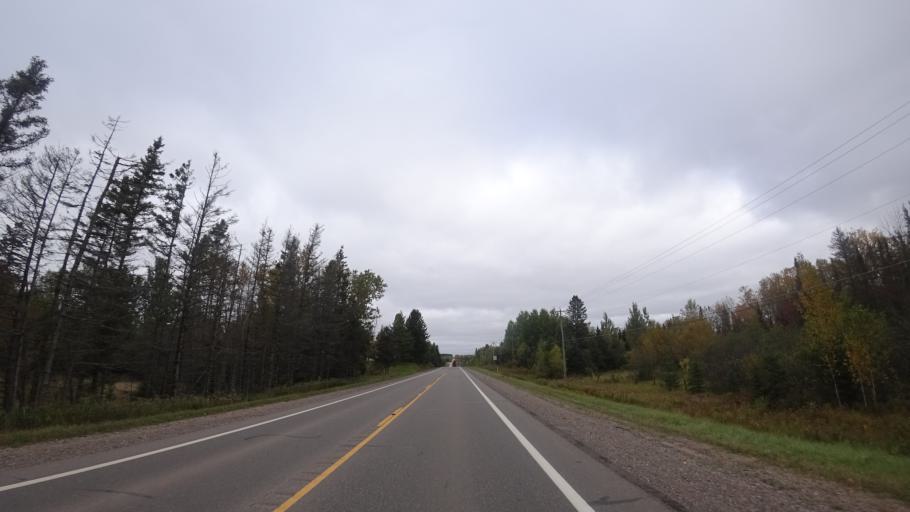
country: US
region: Wisconsin
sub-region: Florence County
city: Florence
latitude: 46.0978
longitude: -88.0757
